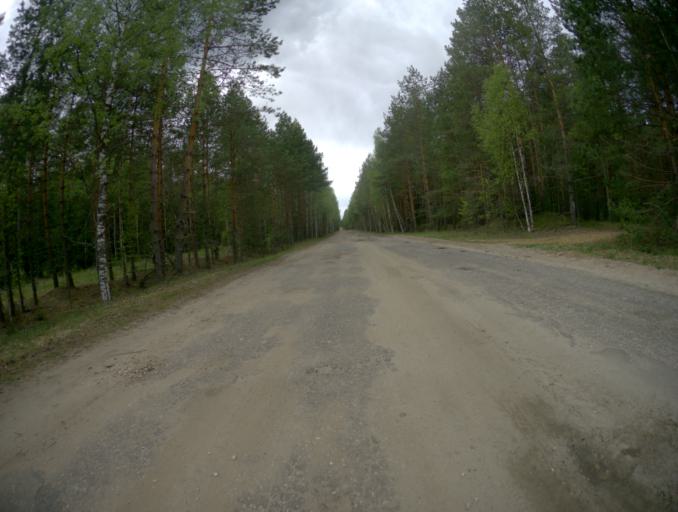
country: RU
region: Vladimir
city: Velikodvorskiy
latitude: 55.2440
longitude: 40.7254
